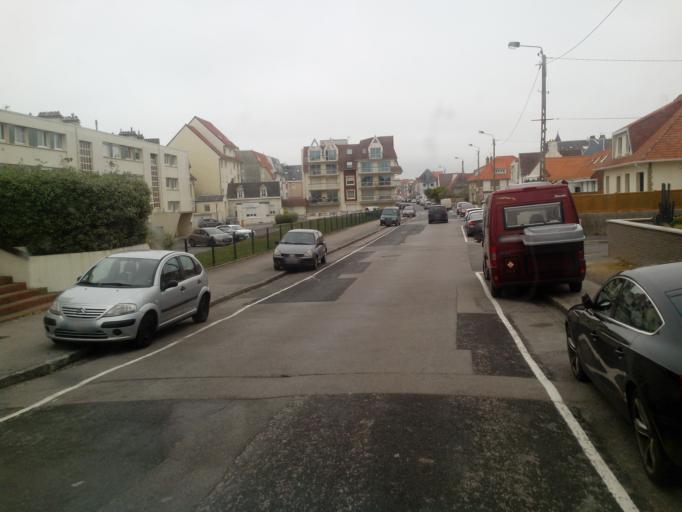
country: FR
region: Nord-Pas-de-Calais
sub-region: Departement du Pas-de-Calais
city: Wimereux
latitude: 50.7633
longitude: 1.6065
